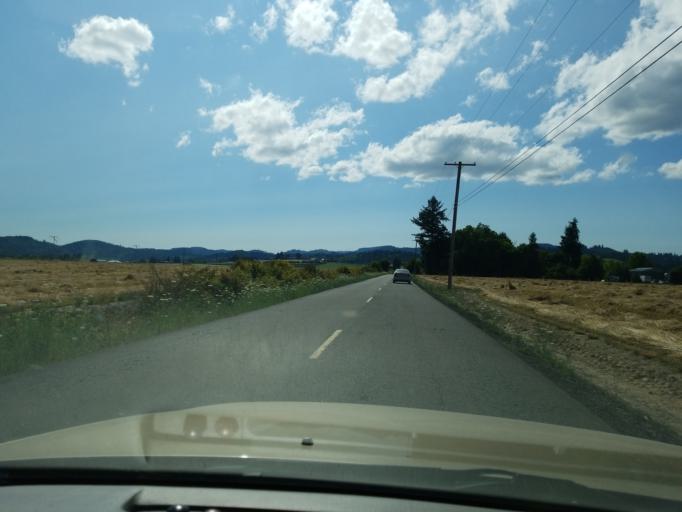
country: US
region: Oregon
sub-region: Yamhill County
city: McMinnville
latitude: 45.2449
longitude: -123.2062
